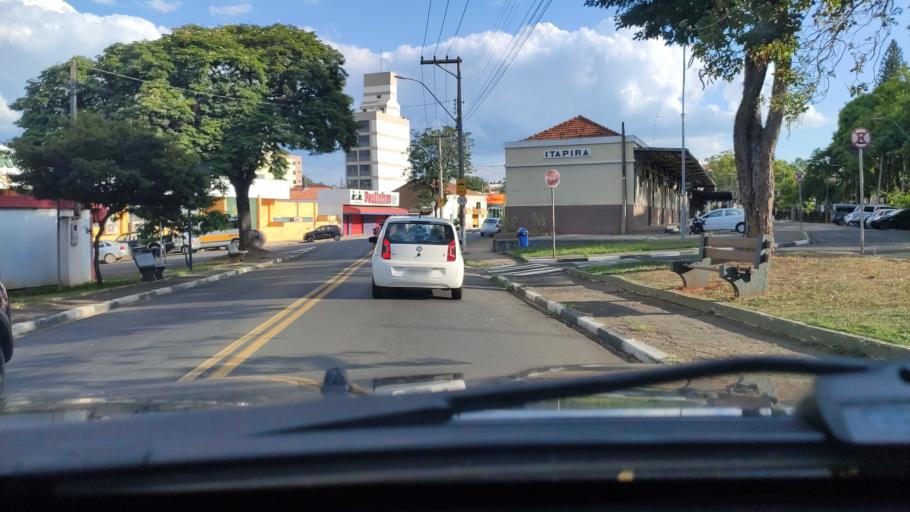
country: BR
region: Sao Paulo
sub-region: Itapira
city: Itapira
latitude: -22.4368
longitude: -46.8255
